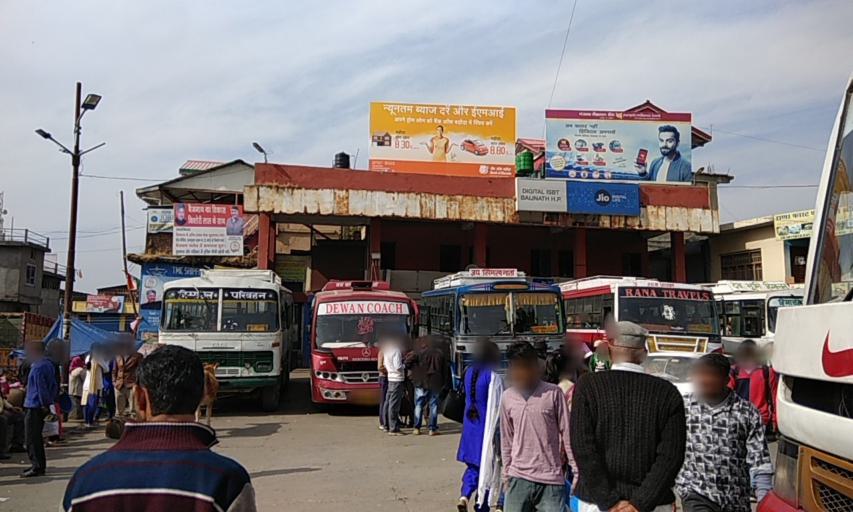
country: IN
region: Himachal Pradesh
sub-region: Kangra
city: Palampur
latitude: 32.0498
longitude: 76.6469
